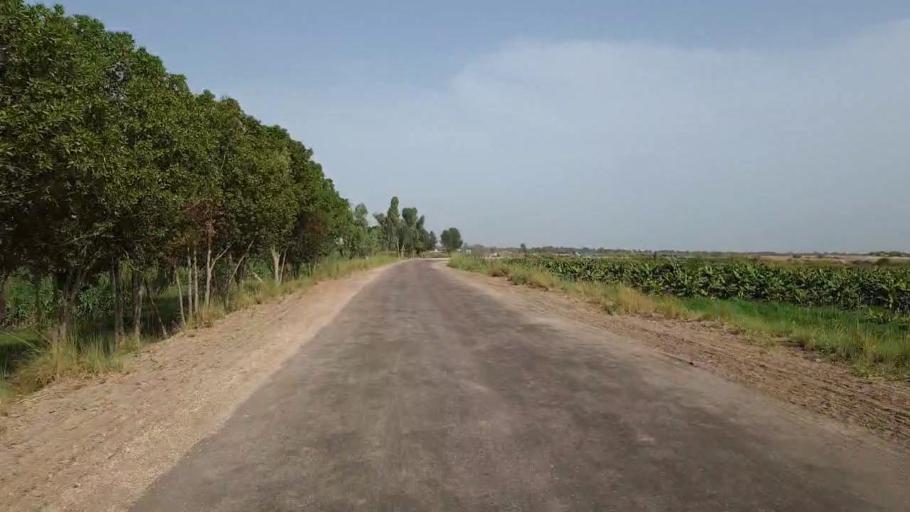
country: PK
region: Sindh
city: Sakrand
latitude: 26.2789
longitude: 68.2699
